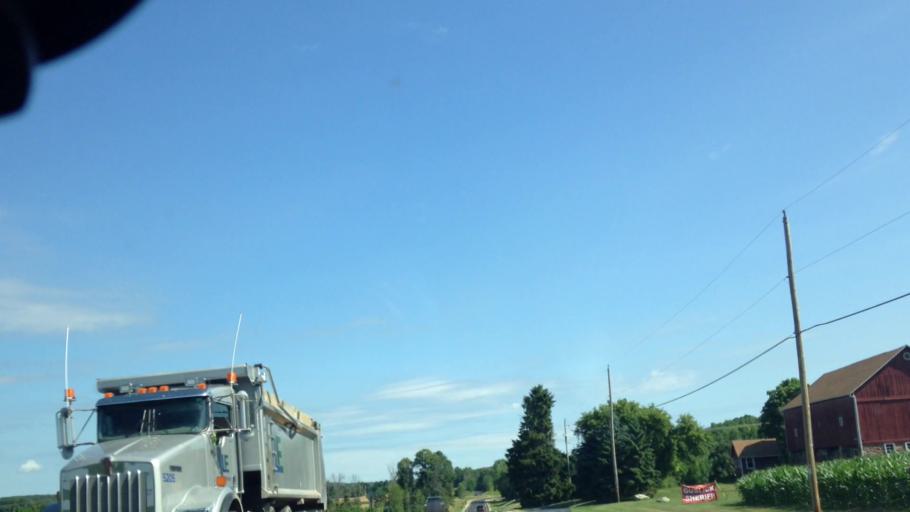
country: US
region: Wisconsin
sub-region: Washington County
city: Slinger
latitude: 43.3574
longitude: -88.2609
